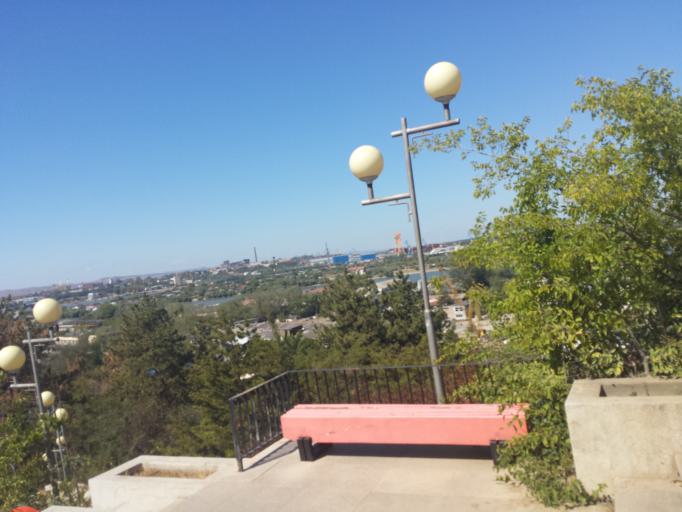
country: RO
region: Tulcea
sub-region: Municipiul Tulcea
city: Tulcea
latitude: 45.1865
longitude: 28.8146
